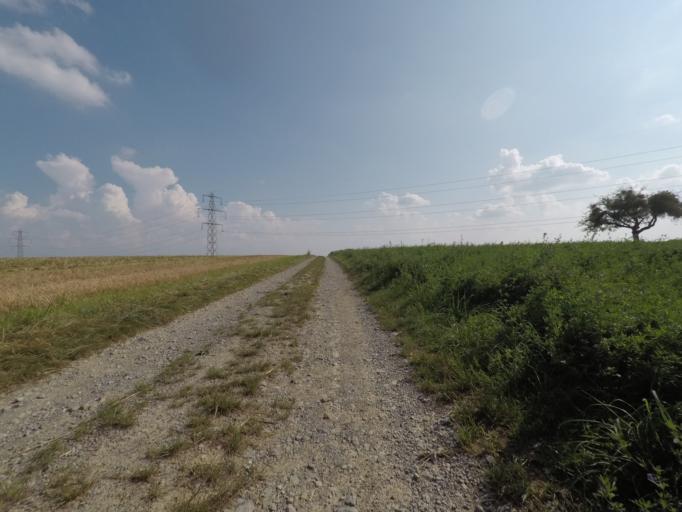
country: DE
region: Baden-Wuerttemberg
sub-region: Regierungsbezirk Stuttgart
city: Weil im Schonbuch
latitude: 48.6350
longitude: 9.0655
